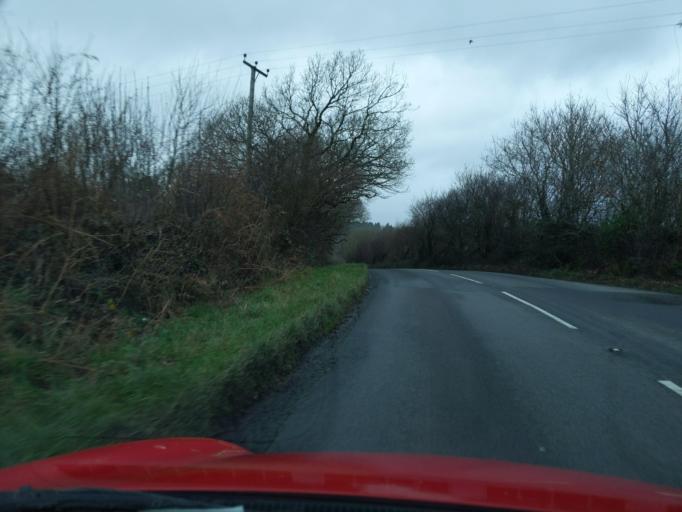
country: GB
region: England
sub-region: Devon
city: Holsworthy
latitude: 50.7803
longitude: -4.3349
